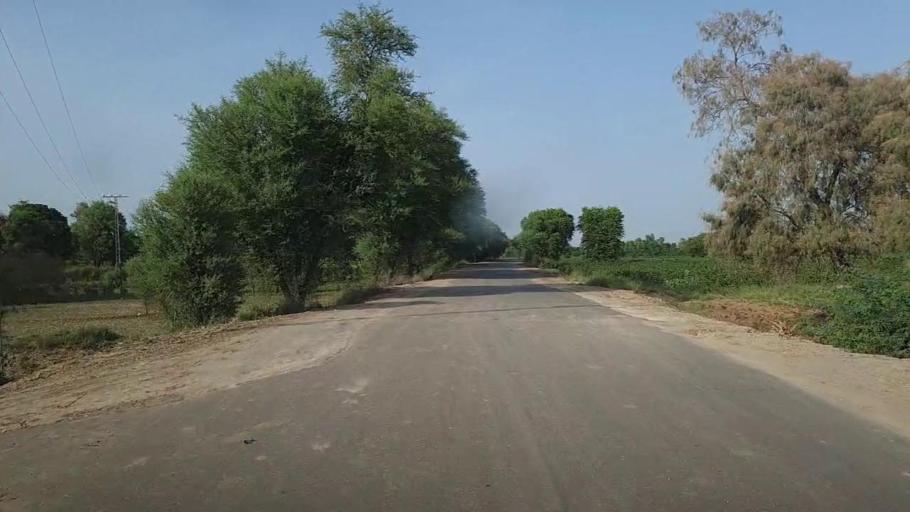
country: PK
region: Sindh
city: Ubauro
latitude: 28.1042
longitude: 69.8459
